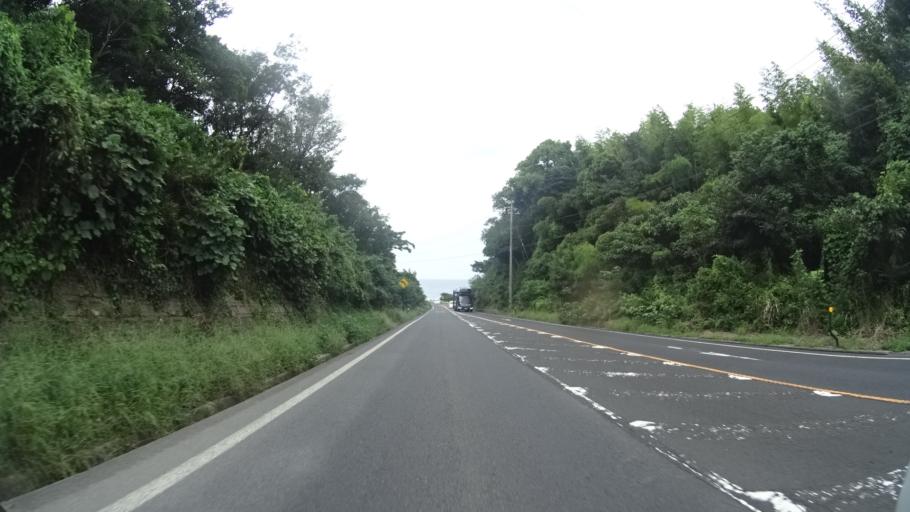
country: JP
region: Shimane
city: Odacho-oda
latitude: 35.1963
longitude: 132.4497
